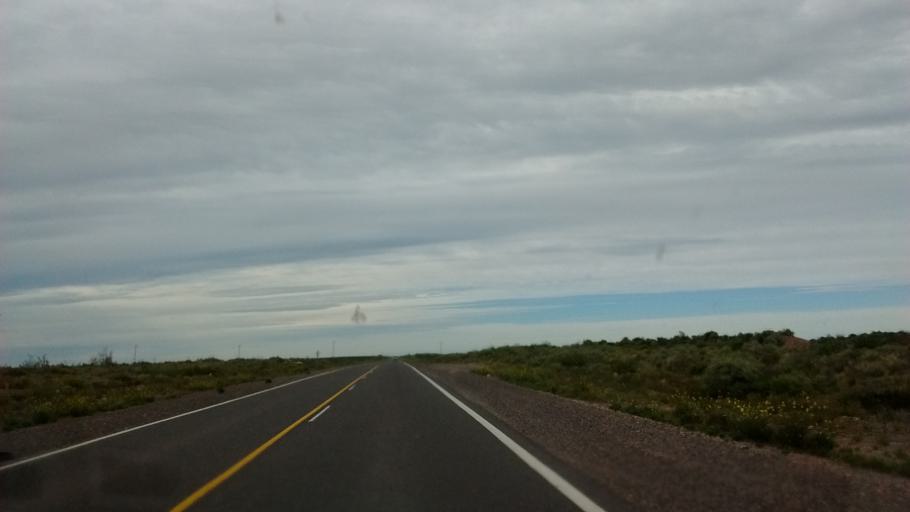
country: AR
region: Rio Negro
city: Catriel
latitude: -38.2183
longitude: -67.9788
